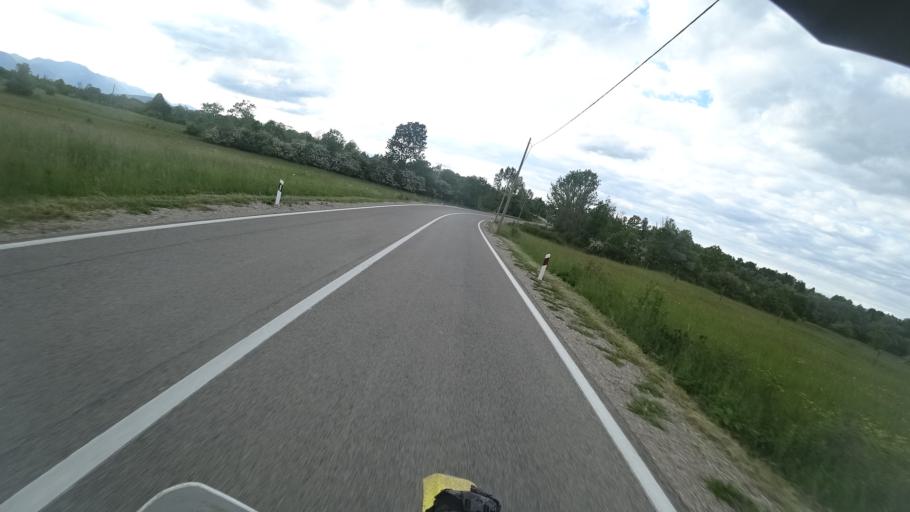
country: HR
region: Licko-Senjska
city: Gospic
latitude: 44.4843
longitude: 15.4678
